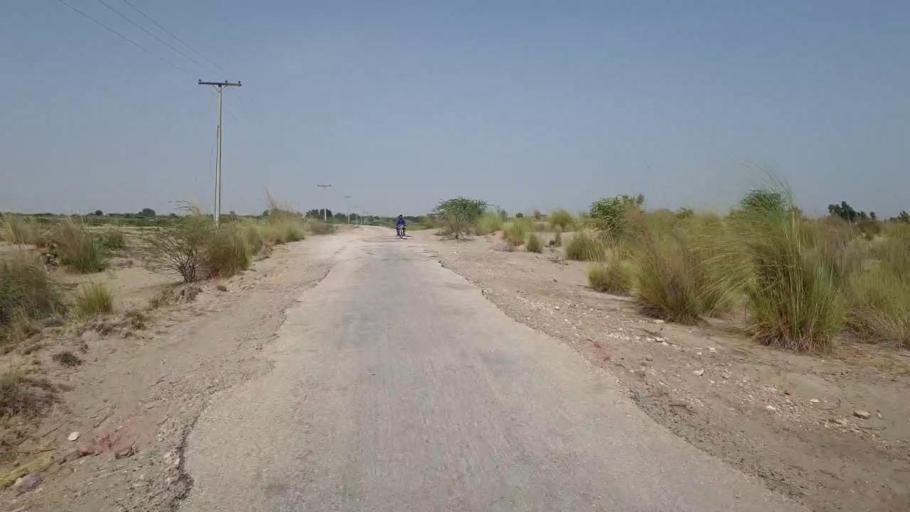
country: PK
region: Sindh
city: Jam Sahib
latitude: 26.4087
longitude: 68.8986
